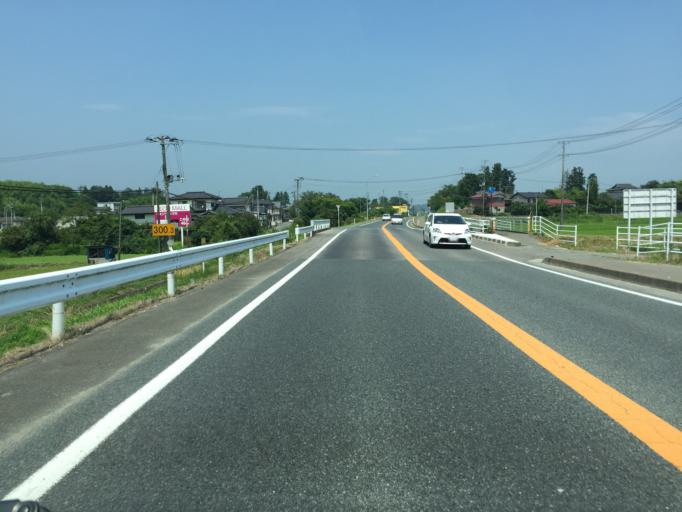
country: JP
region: Miyagi
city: Marumori
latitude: 37.8217
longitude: 140.9200
